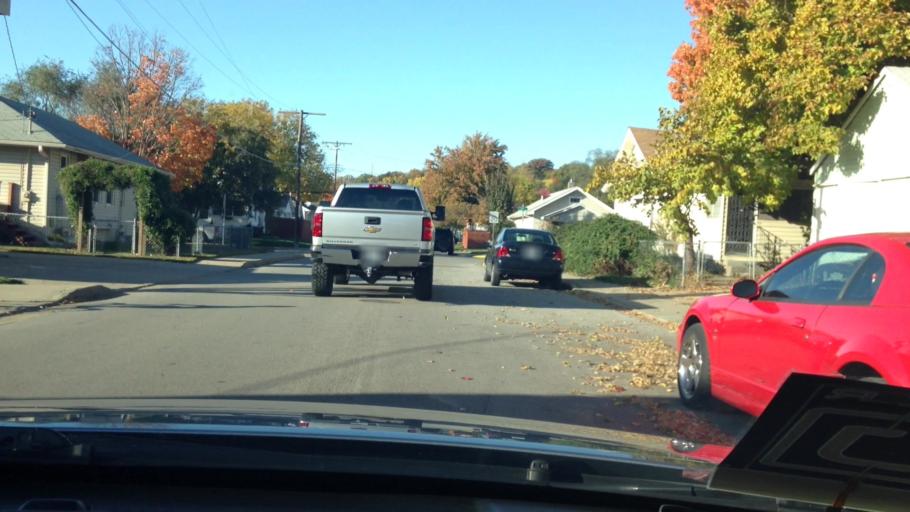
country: US
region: Missouri
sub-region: Clay County
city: North Kansas City
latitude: 39.1457
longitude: -94.5673
